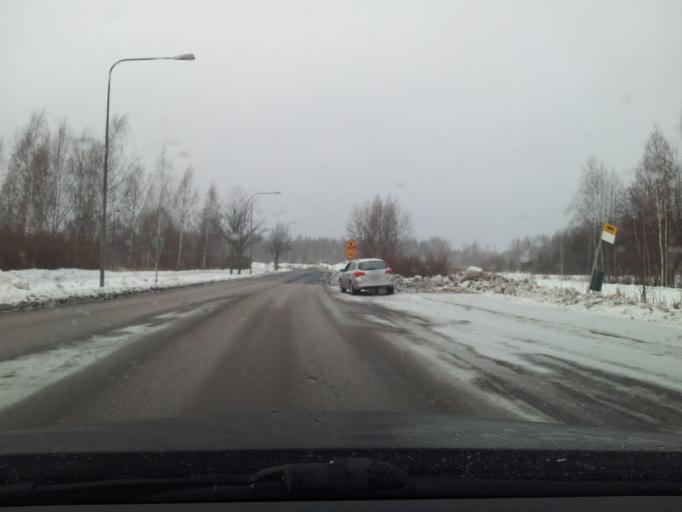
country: FI
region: Uusimaa
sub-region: Helsinki
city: Koukkuniemi
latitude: 60.1832
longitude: 24.7779
